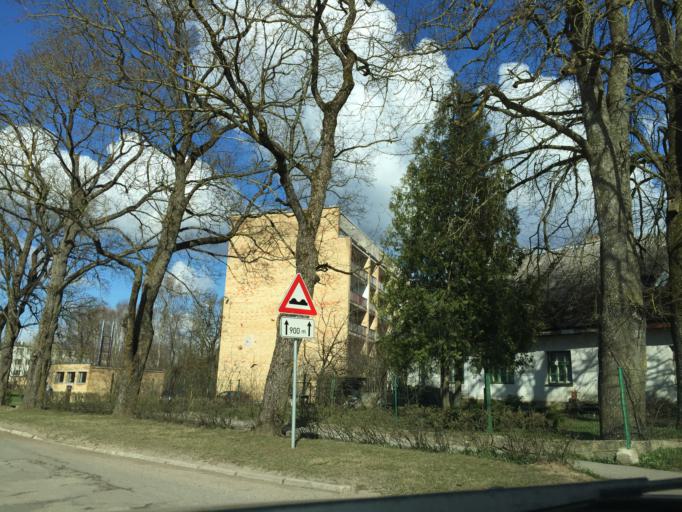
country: LV
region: Kekava
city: Kekava
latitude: 56.8248
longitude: 24.2293
